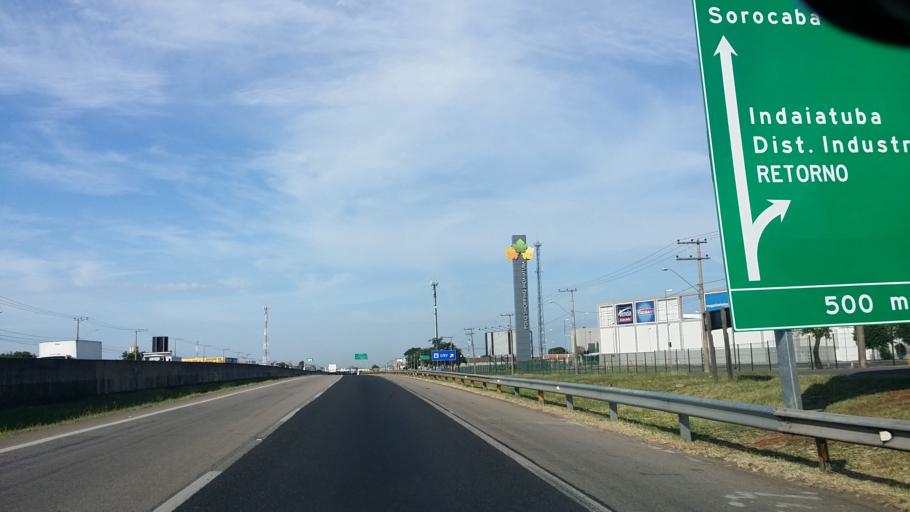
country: BR
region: Sao Paulo
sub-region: Indaiatuba
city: Indaiatuba
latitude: -23.1174
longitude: -47.2175
